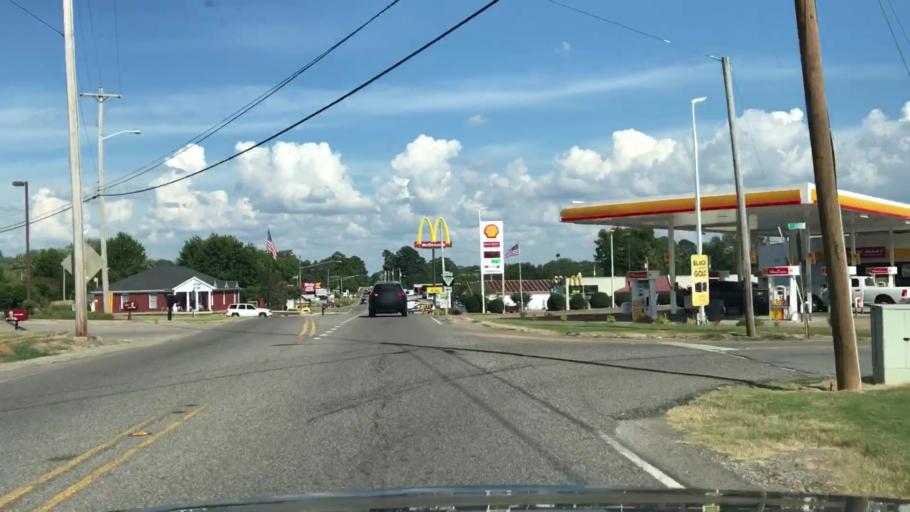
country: US
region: Tennessee
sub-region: Giles County
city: Ardmore
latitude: 34.9944
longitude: -86.8422
